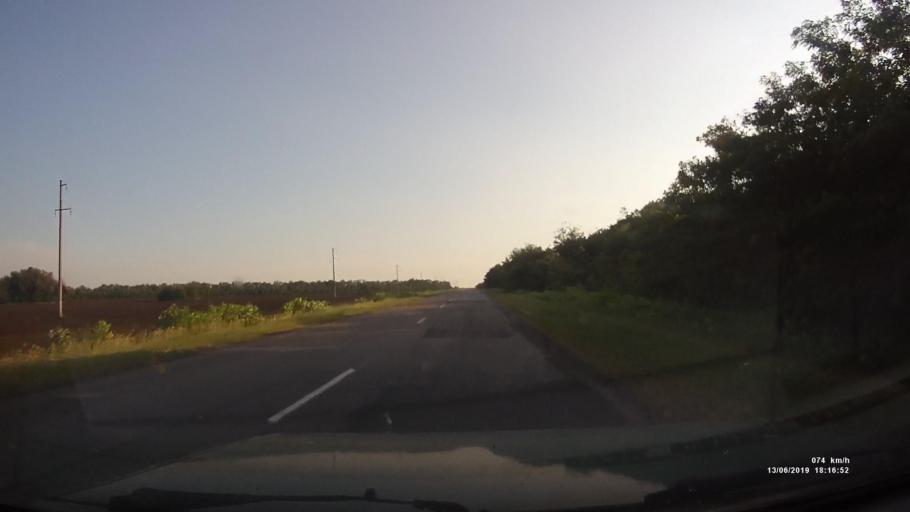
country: RU
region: Rostov
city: Kazanskaya
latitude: 49.9248
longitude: 41.3328
